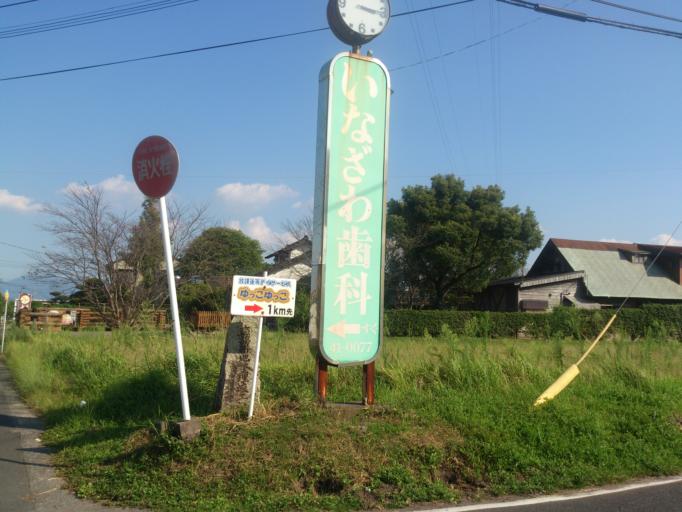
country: JP
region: Kagoshima
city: Kanoya
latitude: 31.3613
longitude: 130.8714
